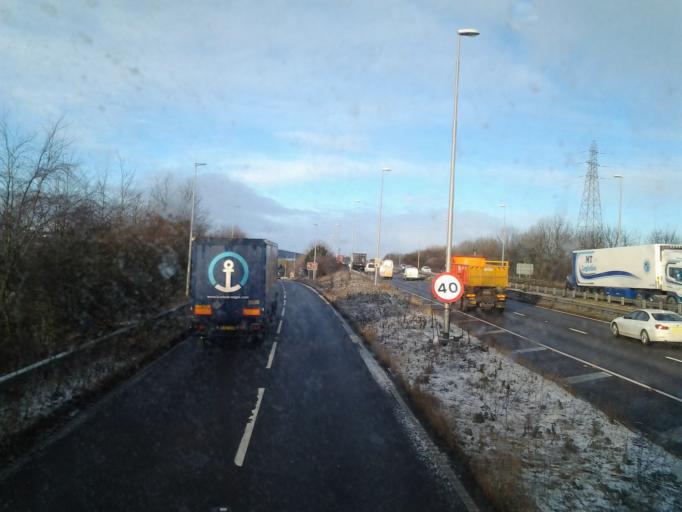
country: GB
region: England
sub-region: Gateshead
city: Lamesley
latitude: 54.9100
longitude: -1.5792
